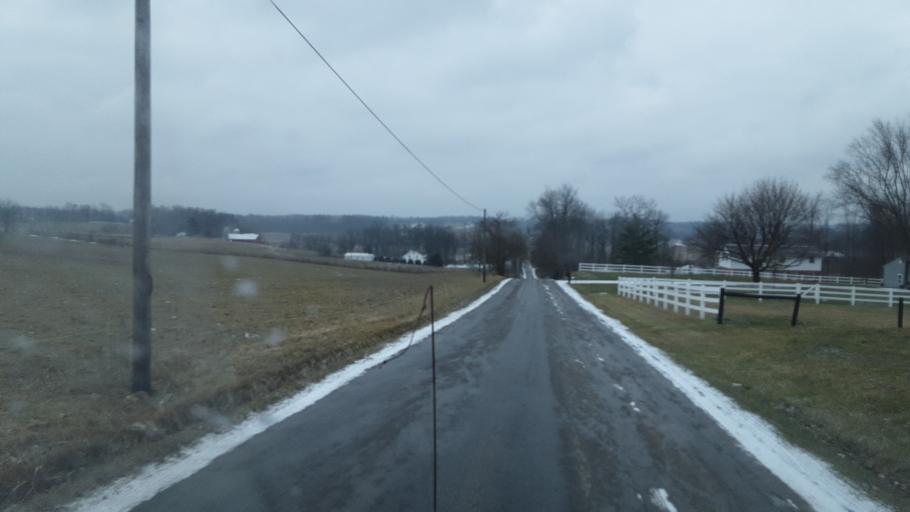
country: US
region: Ohio
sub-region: Wayne County
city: Apple Creek
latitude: 40.6410
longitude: -81.7457
